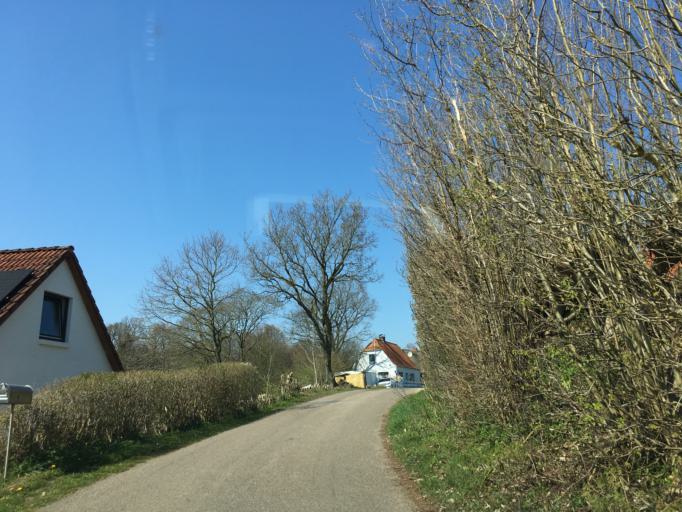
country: DE
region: Schleswig-Holstein
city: Nottfeld
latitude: 54.5946
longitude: 9.7997
